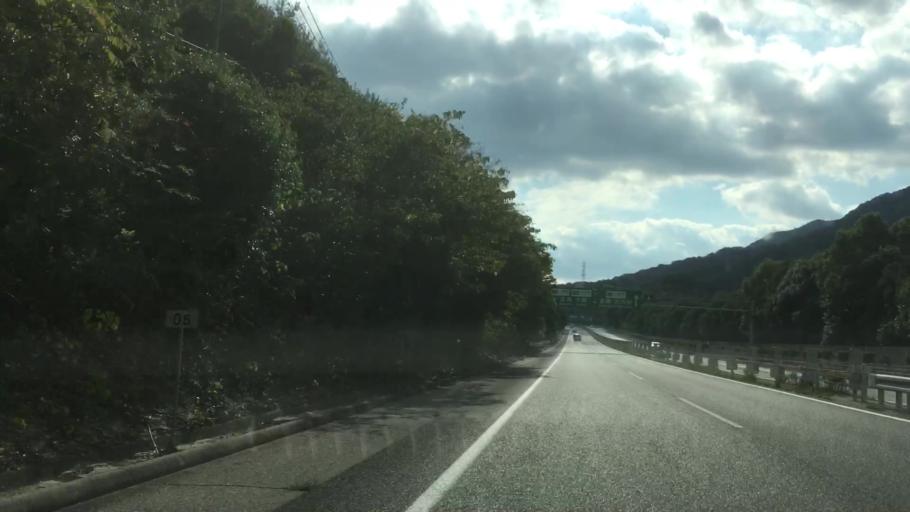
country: JP
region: Hiroshima
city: Hatsukaichi
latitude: 34.3418
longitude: 132.3027
